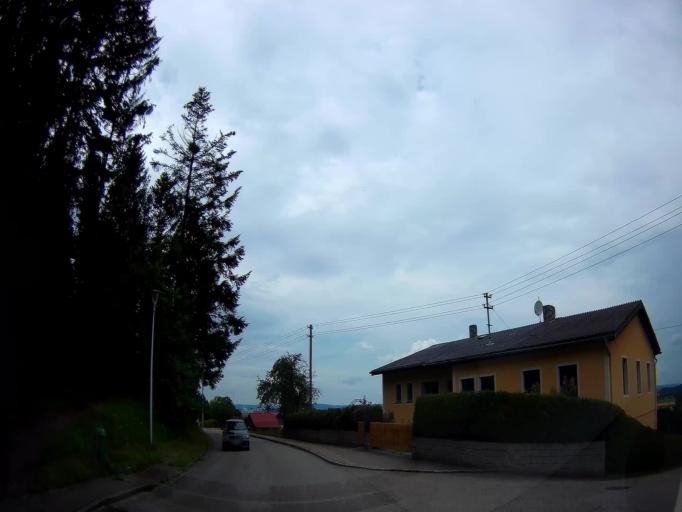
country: AT
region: Upper Austria
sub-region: Politischer Bezirk Braunau am Inn
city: Altheim
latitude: 48.2661
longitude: 13.3007
